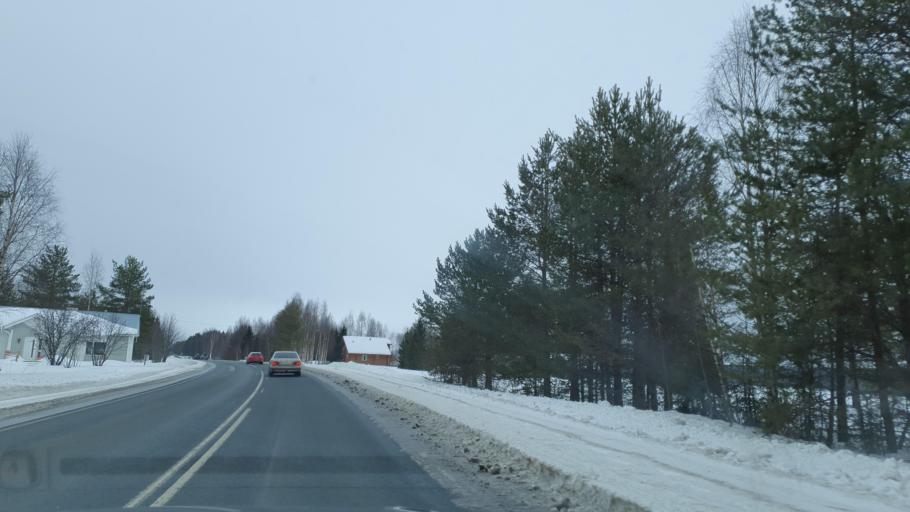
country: FI
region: Lapland
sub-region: Torniolaakso
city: Pello
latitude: 66.6100
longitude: 23.8879
